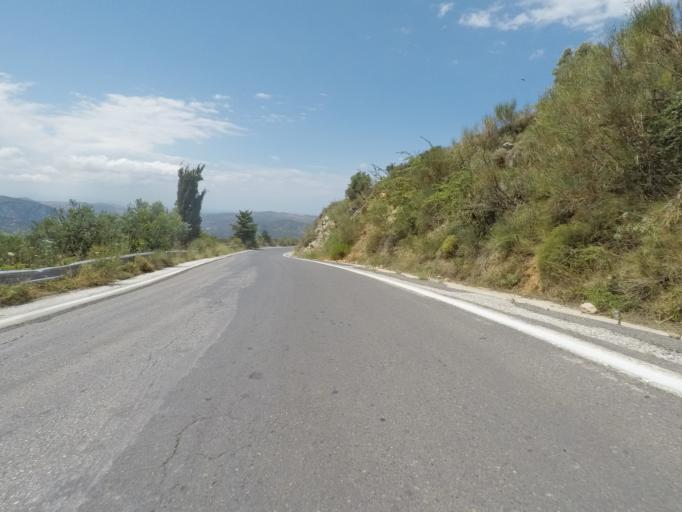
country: GR
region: Crete
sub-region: Nomos Irakleiou
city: Mokhos
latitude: 35.2163
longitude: 25.4592
